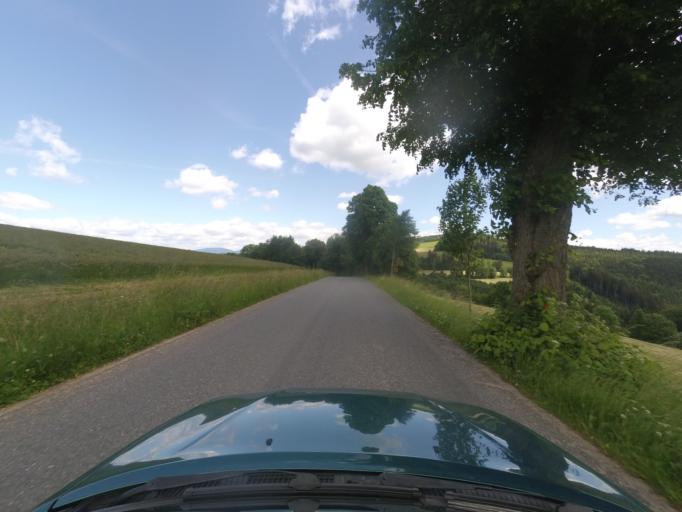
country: CZ
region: Pardubicky
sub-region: Okres Usti nad Orlici
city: Kunvald
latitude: 50.1157
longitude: 16.5837
